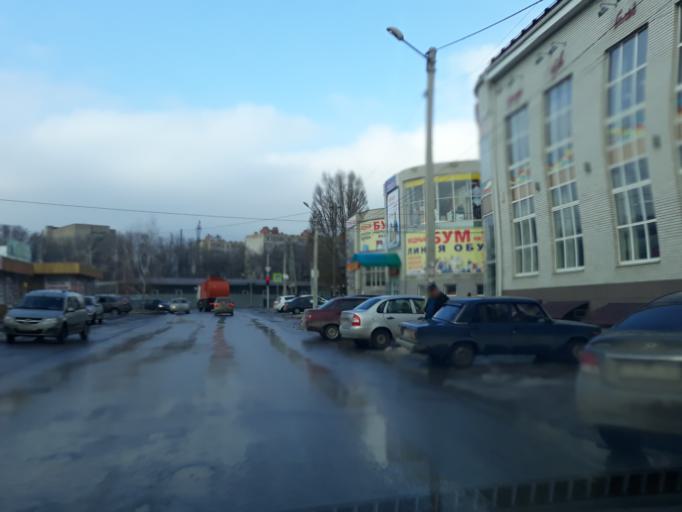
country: RU
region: Rostov
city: Taganrog
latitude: 47.2592
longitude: 38.9121
